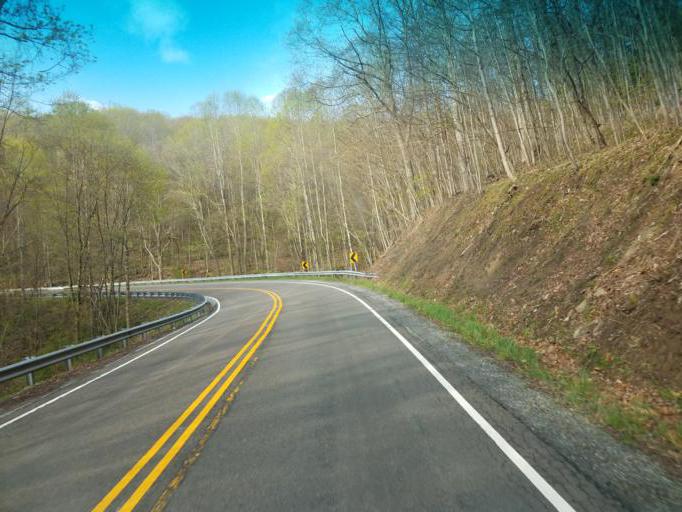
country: US
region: Virginia
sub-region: Smyth County
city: Atkins
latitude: 36.8119
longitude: -81.4258
